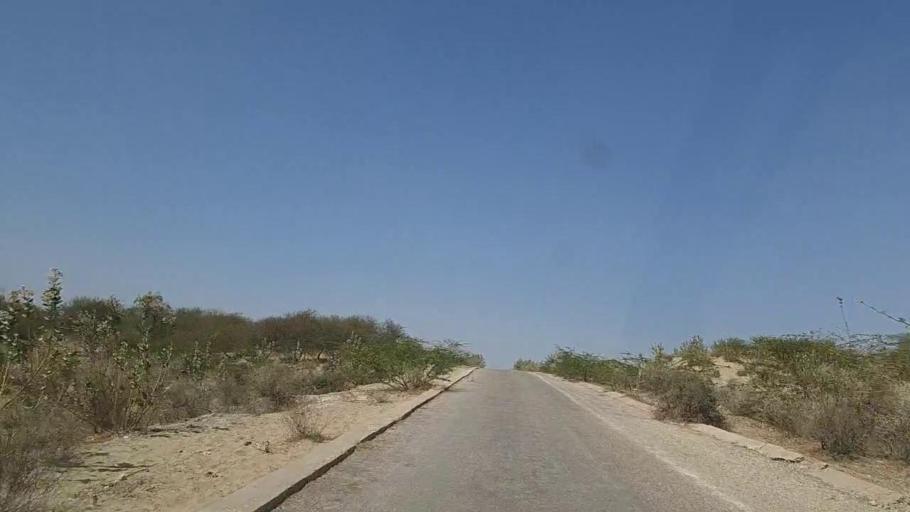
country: PK
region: Sindh
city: Diplo
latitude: 24.5815
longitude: 69.3198
